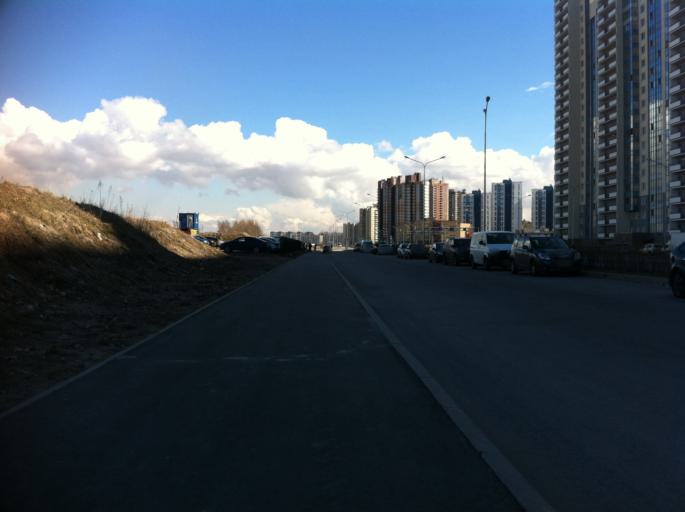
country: RU
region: St.-Petersburg
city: Uritsk
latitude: 59.8667
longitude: 30.1784
